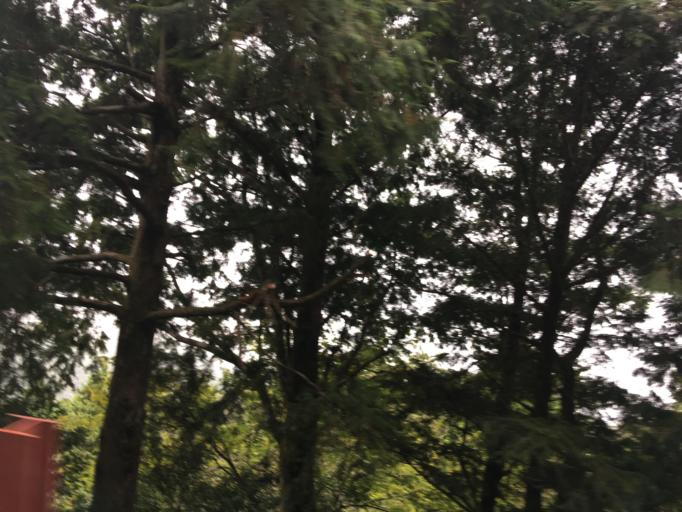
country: TW
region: Taiwan
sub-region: Yilan
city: Yilan
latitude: 24.4880
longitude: 121.5344
